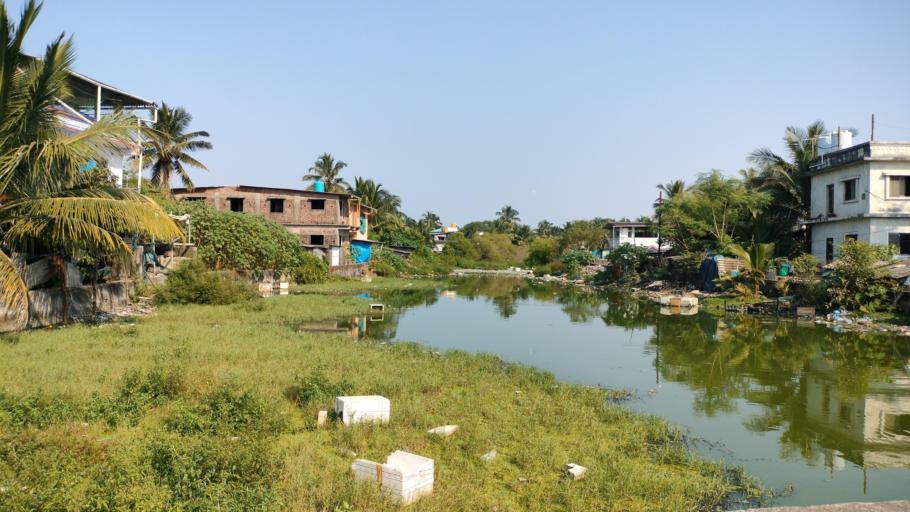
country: IN
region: Maharashtra
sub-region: Thane
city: Bhayandar
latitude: 19.3274
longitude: 72.8105
